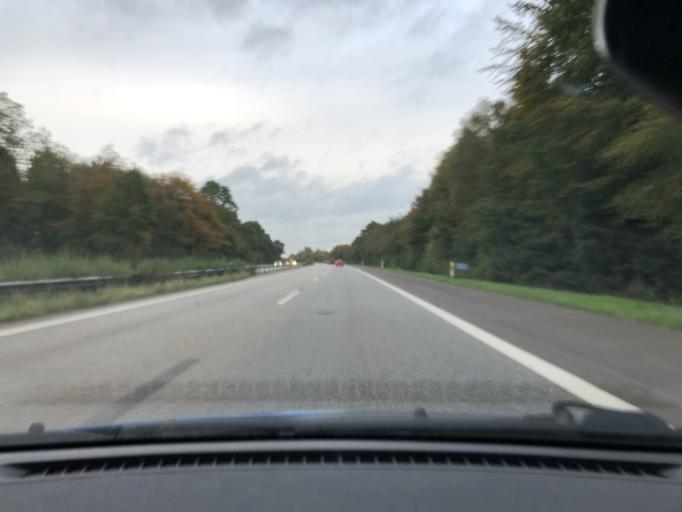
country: DE
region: Schleswig-Holstein
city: Mielkendorf
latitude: 54.2744
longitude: 10.0467
